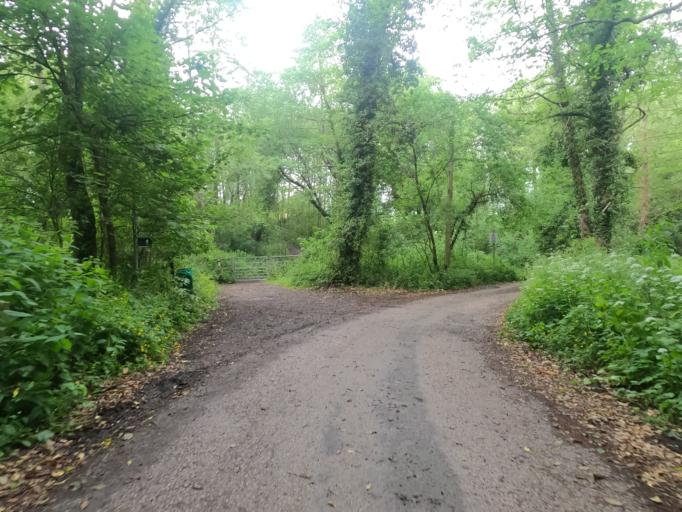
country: GB
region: England
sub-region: Cheshire West and Chester
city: Cuddington
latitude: 53.2364
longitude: -2.6132
